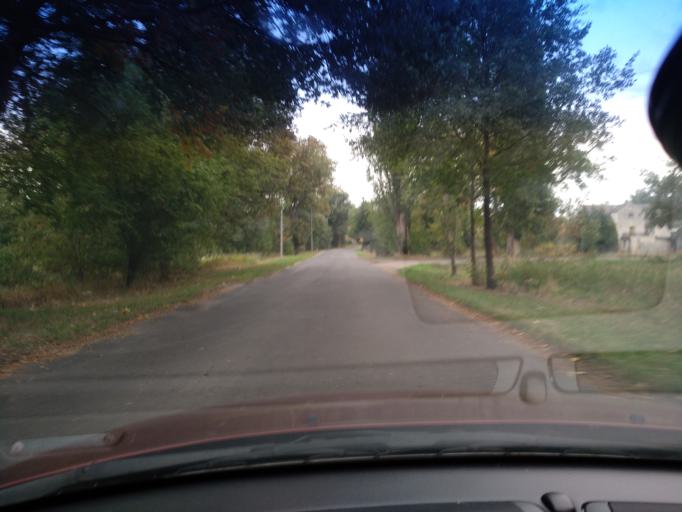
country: PL
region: Lower Silesian Voivodeship
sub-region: Powiat zgorzelecki
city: Zgorzelec
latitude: 51.1872
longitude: 15.0139
